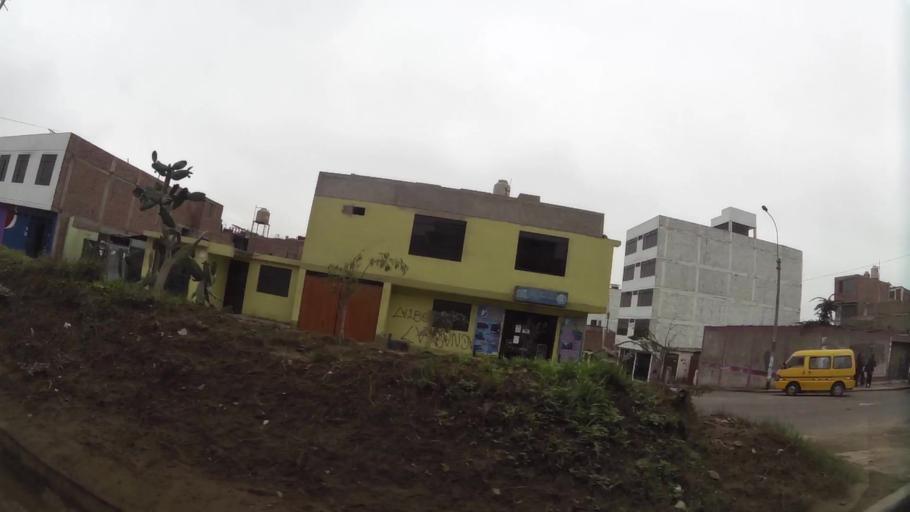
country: PE
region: Lima
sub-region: Lima
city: Surco
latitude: -12.1685
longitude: -76.9612
